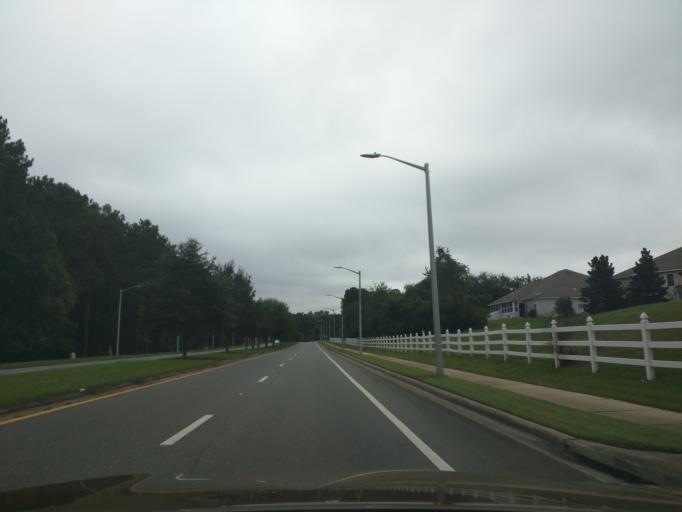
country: US
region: Florida
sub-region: Leon County
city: Tallahassee
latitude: 30.4352
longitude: -84.2012
